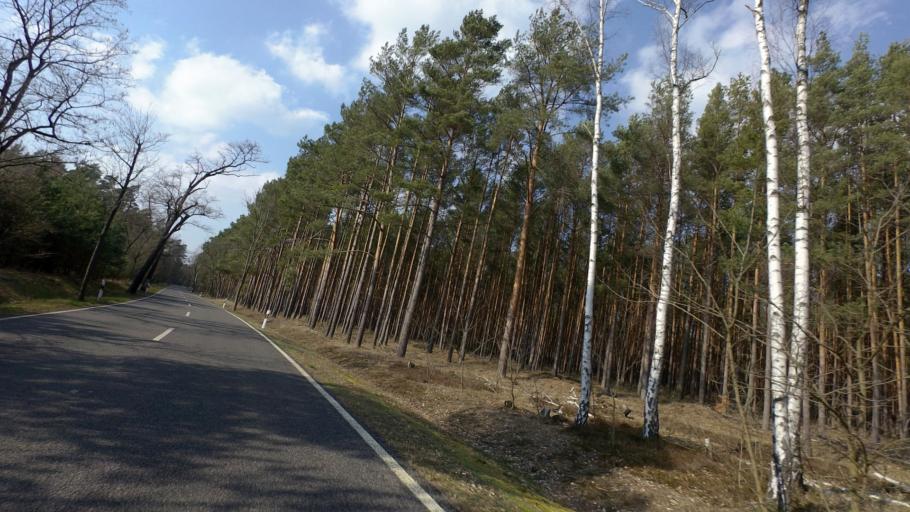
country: DE
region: Brandenburg
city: Dahme
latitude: 51.9269
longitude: 13.4642
